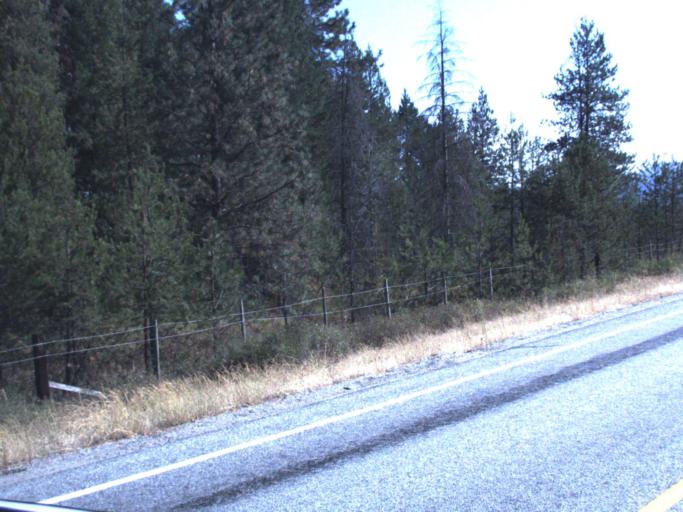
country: US
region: Washington
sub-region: Pend Oreille County
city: Newport
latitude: 48.2570
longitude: -117.2845
